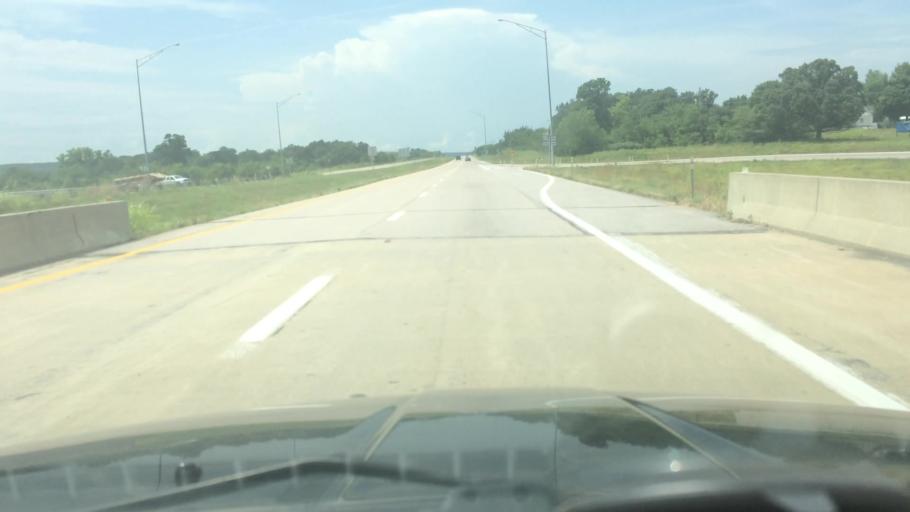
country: US
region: Missouri
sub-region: Polk County
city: Humansville
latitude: 37.7944
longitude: -93.5887
